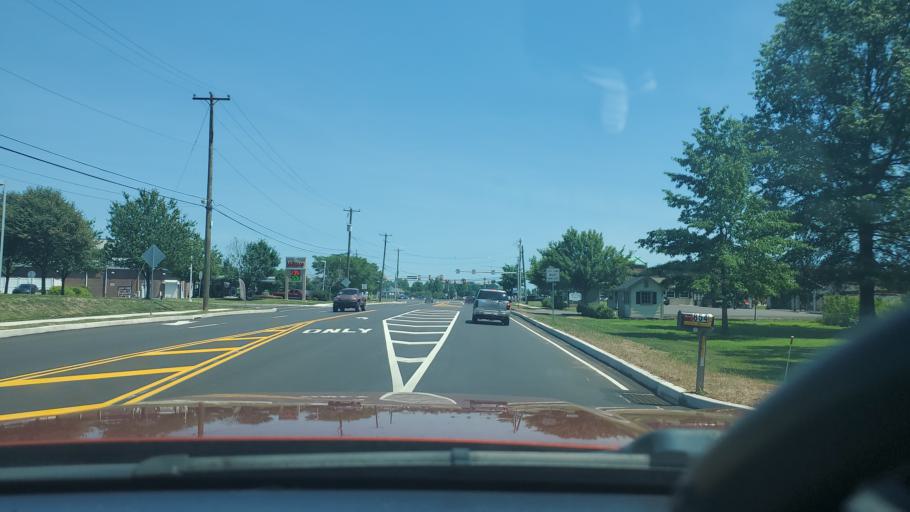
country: US
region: Pennsylvania
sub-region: Montgomery County
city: Limerick
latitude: 40.2312
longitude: -75.5287
